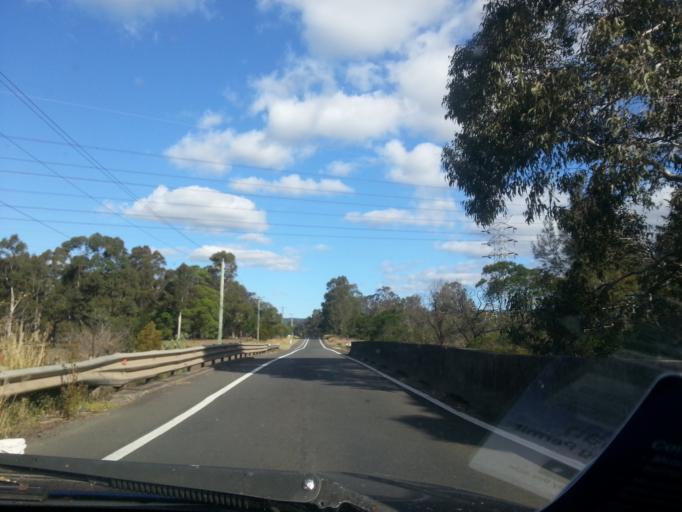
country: AU
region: New South Wales
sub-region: Wollongong
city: Dapto
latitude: -34.5268
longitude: 150.7887
